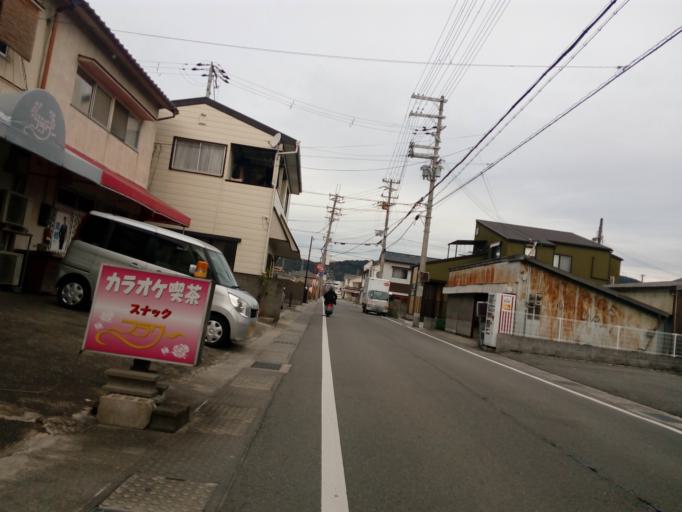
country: JP
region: Hyogo
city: Tatsunocho-tominaga
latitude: 34.7991
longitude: 134.6065
